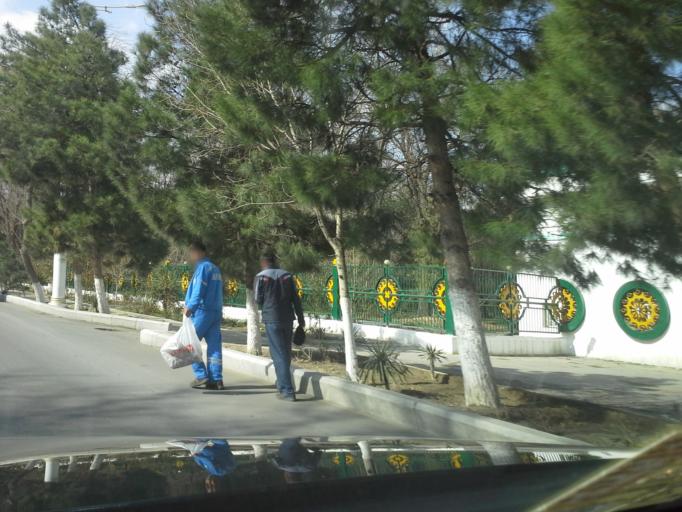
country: TM
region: Ahal
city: Ashgabat
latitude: 37.9494
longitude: 58.3467
